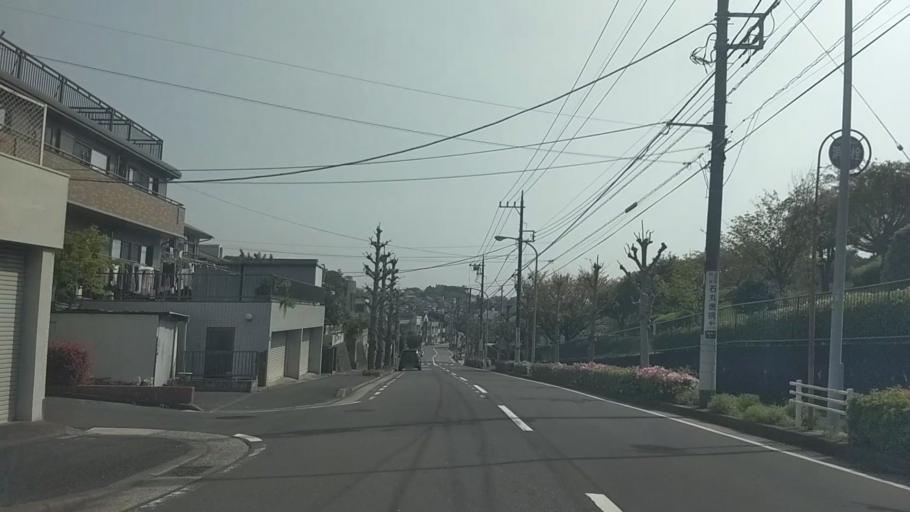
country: JP
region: Kanagawa
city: Zushi
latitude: 35.3644
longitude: 139.6199
